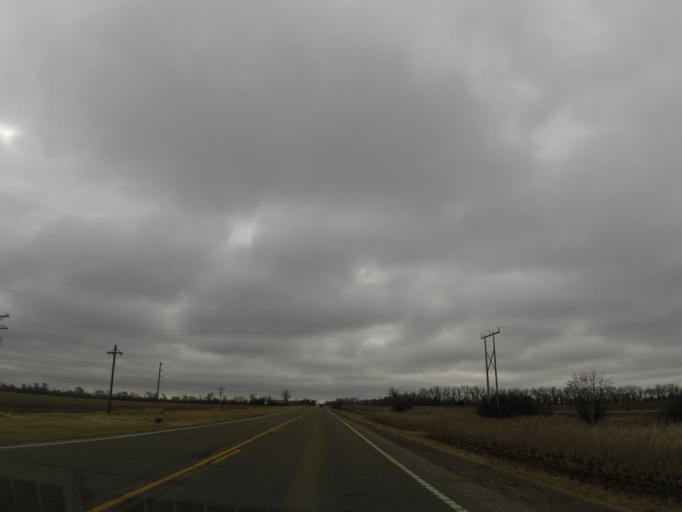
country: US
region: North Dakota
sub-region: Cass County
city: Casselton
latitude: 47.1508
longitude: -97.2176
